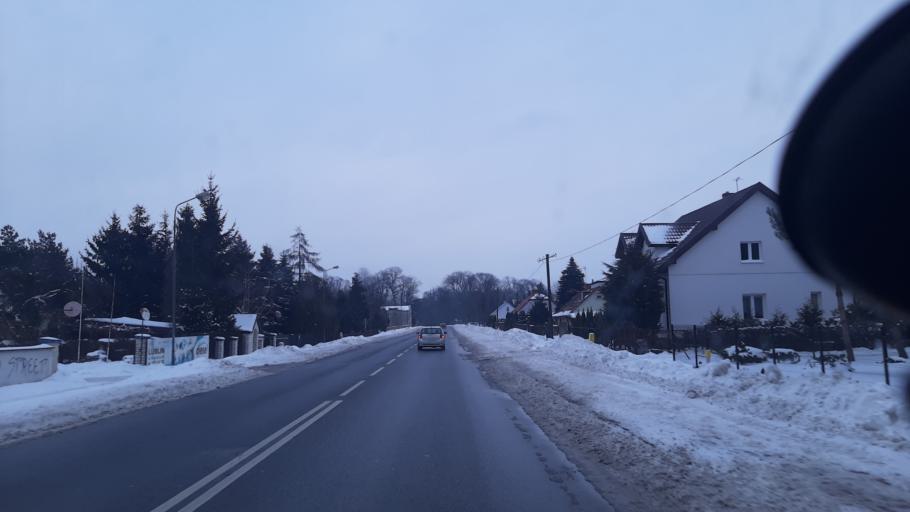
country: PL
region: Lublin Voivodeship
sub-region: Powiat lubelski
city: Garbow
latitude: 51.3563
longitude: 22.3251
